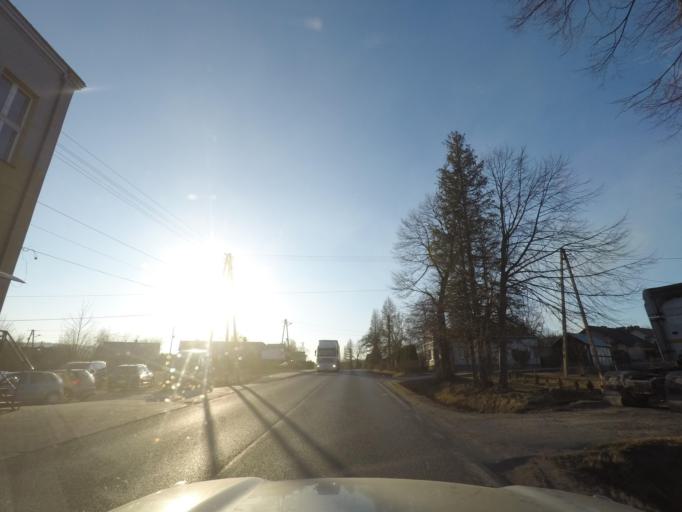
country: PL
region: Subcarpathian Voivodeship
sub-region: Powiat krosnienski
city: Dukla
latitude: 49.5584
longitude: 21.6741
